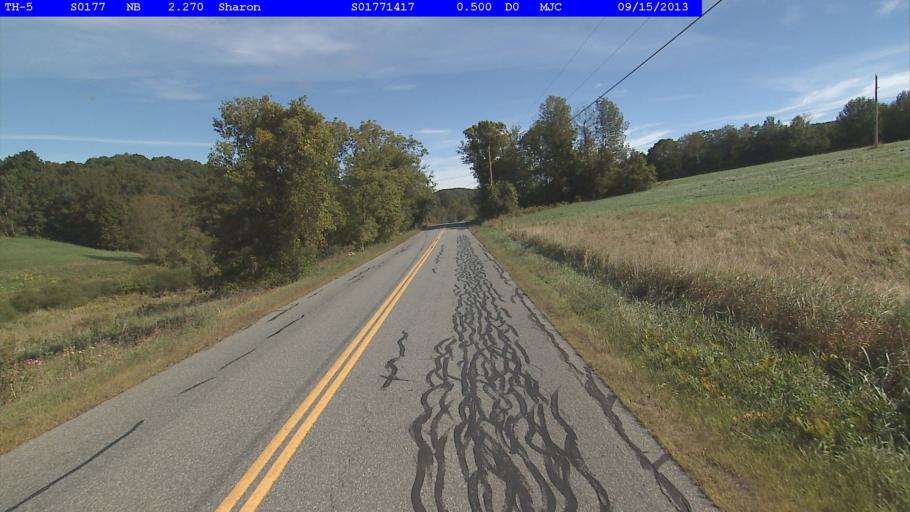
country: US
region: Vermont
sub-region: Windsor County
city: Woodstock
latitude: 43.7513
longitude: -72.4845
